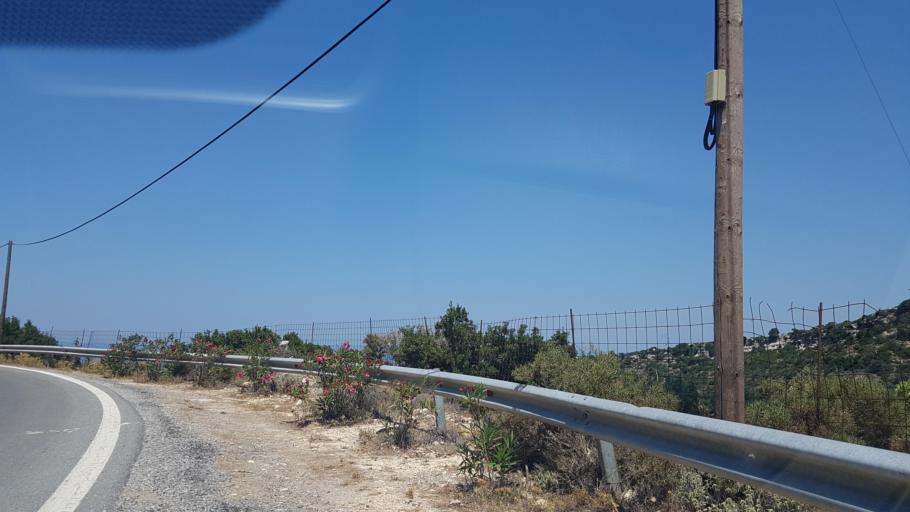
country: GR
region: Crete
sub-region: Nomos Rethymnis
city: Agia Foteini
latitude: 35.3173
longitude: 24.6257
